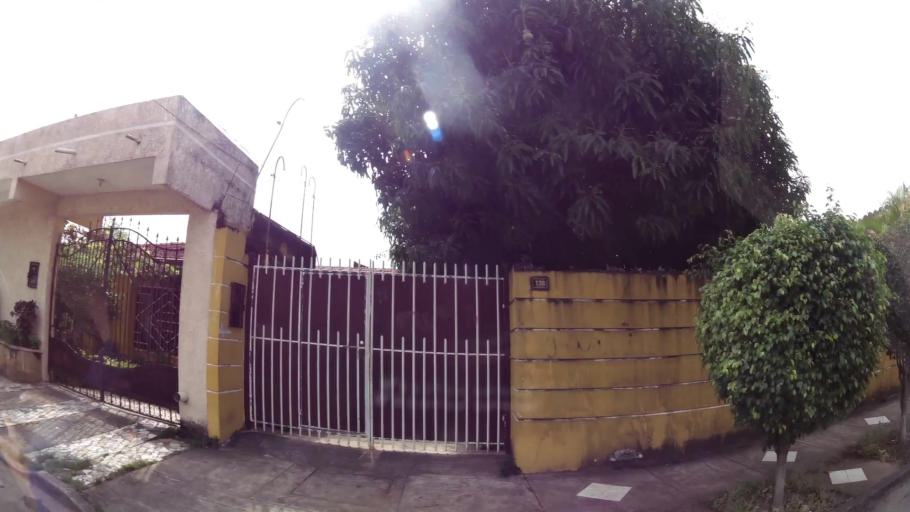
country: BO
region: Santa Cruz
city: Santa Cruz de la Sierra
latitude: -17.7912
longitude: -63.2023
